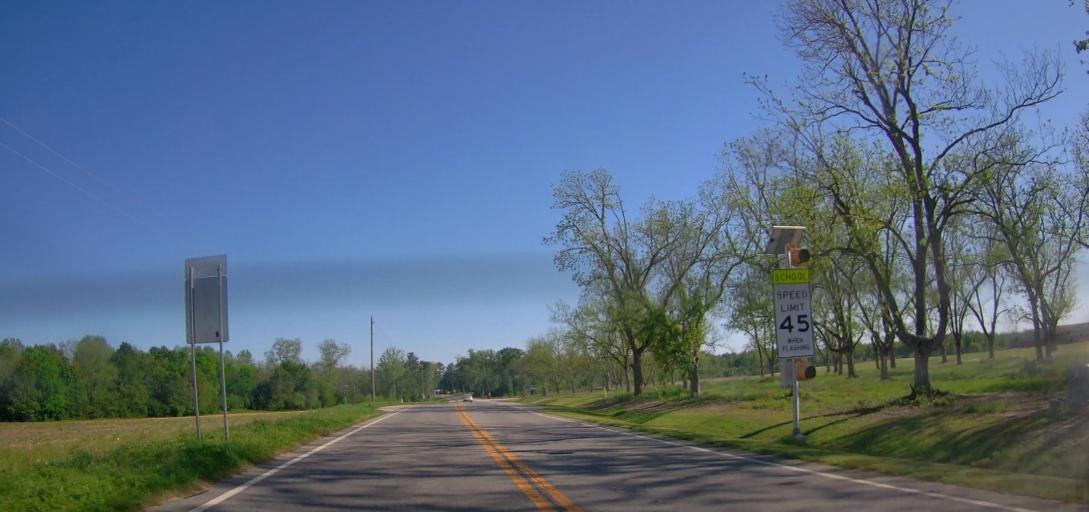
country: US
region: Georgia
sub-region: Wilcox County
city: Rochelle
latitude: 31.9416
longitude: -83.4425
